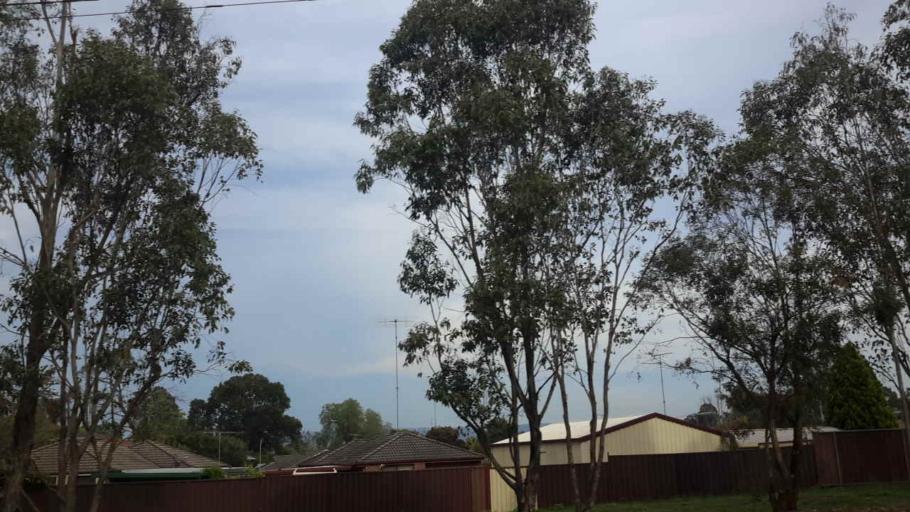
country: AU
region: New South Wales
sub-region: Penrith Municipality
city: Werrington Downs
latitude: -33.7363
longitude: 150.7172
